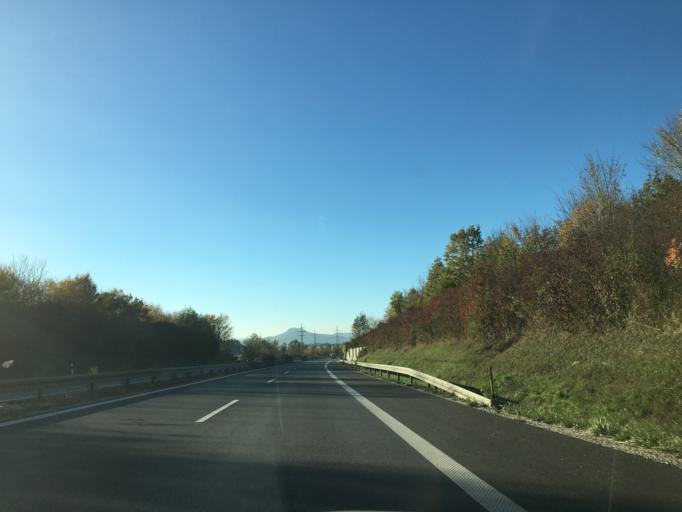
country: DE
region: Baden-Wuerttemberg
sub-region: Freiburg Region
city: Volkertshausen
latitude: 47.7944
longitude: 8.8743
